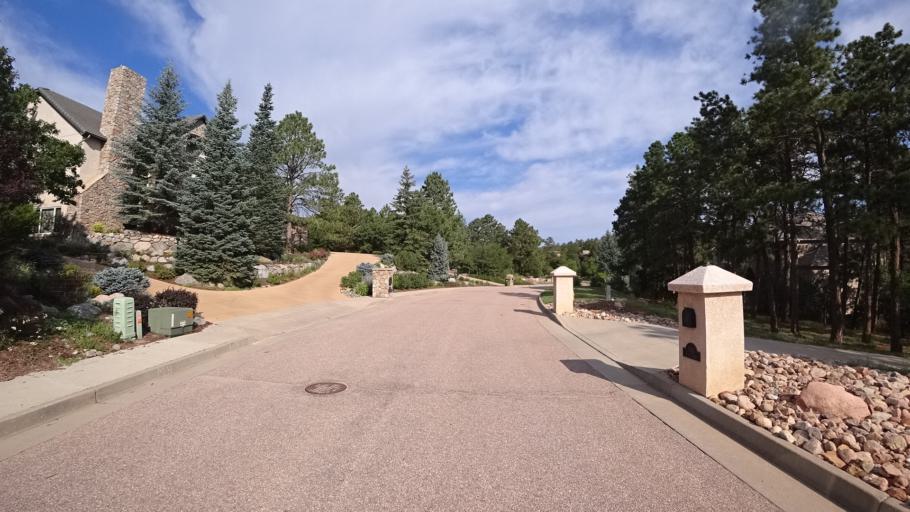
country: US
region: Colorado
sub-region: El Paso County
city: Air Force Academy
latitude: 38.9438
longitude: -104.8271
